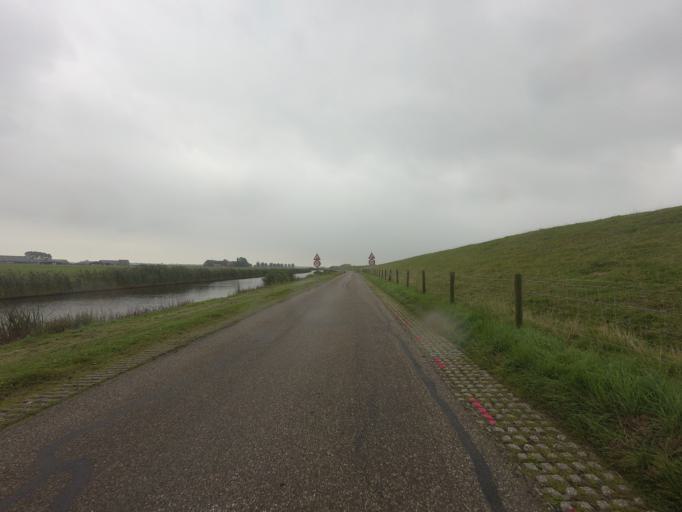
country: NL
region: Friesland
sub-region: Sudwest Fryslan
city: Koudum
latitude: 52.9303
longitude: 5.4061
